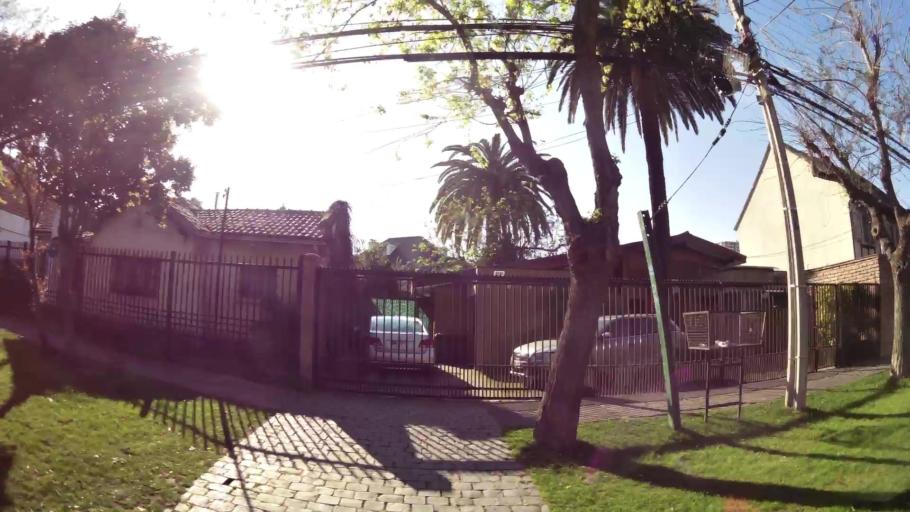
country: CL
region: Santiago Metropolitan
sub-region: Provincia de Santiago
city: Villa Presidente Frei, Nunoa, Santiago, Chile
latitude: -33.4520
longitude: -70.5854
